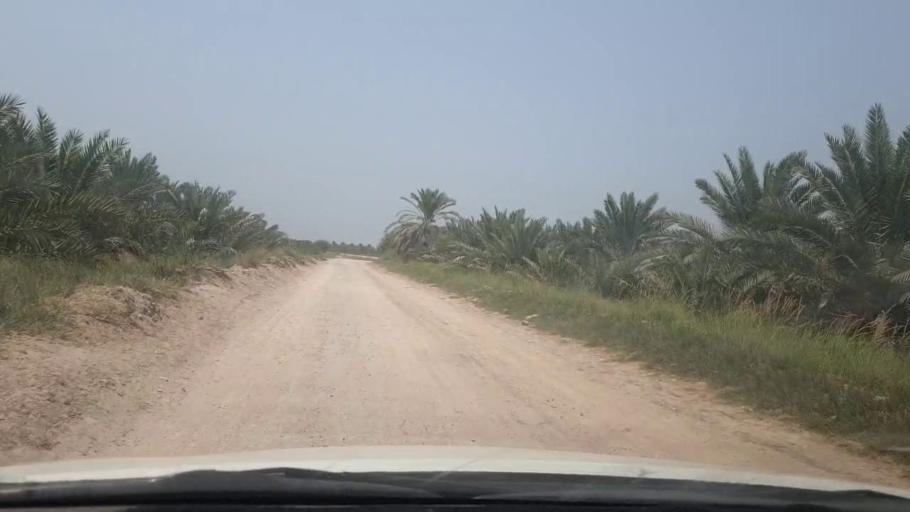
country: PK
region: Sindh
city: Khairpur
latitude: 27.5013
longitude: 68.8717
